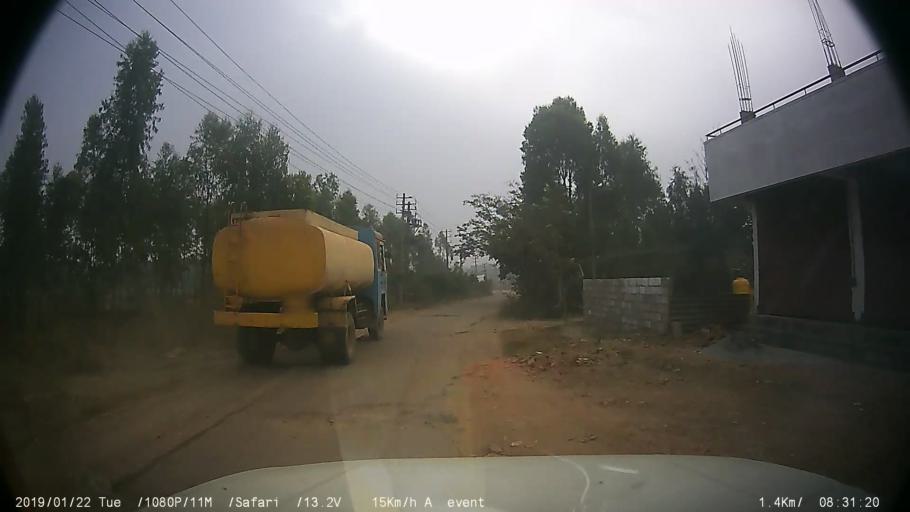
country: IN
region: Karnataka
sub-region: Bangalore Urban
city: Anekal
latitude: 12.8250
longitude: 77.6356
